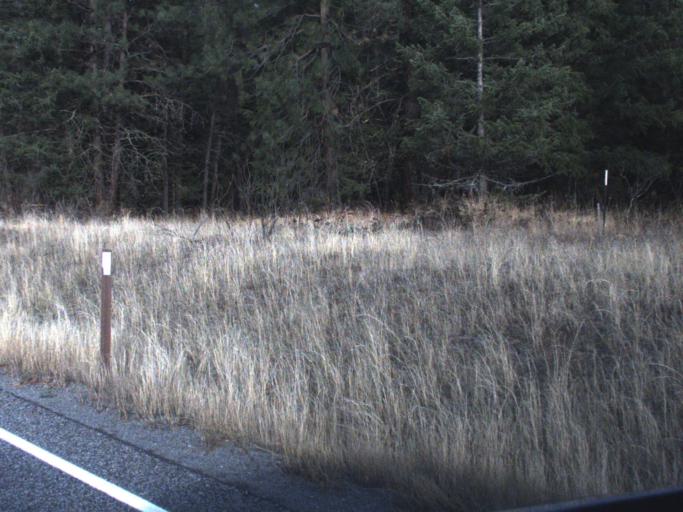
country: CA
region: British Columbia
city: Rossland
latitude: 48.8570
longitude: -117.8787
